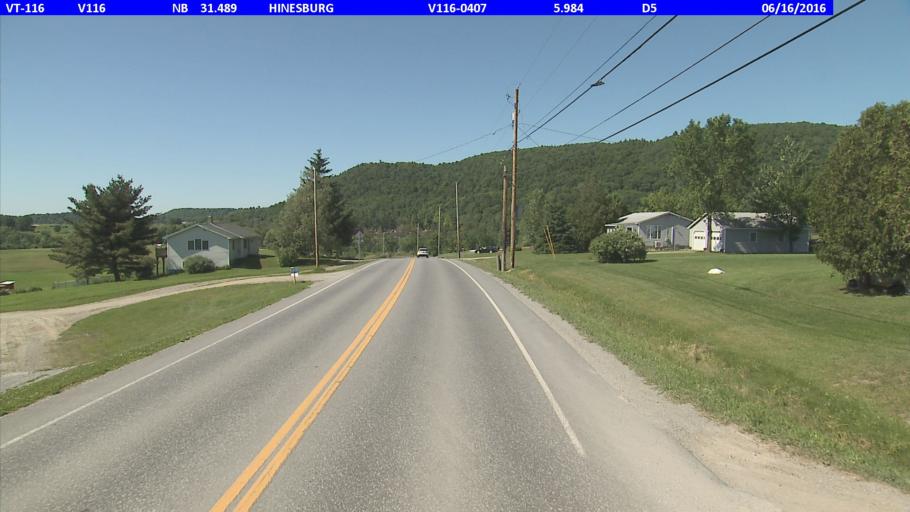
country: US
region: Vermont
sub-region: Chittenden County
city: Hinesburg
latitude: 44.3484
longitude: -73.1179
